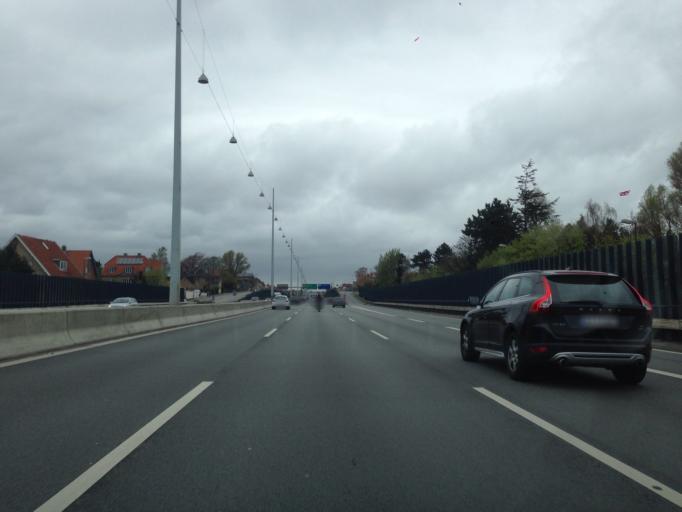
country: DK
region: Capital Region
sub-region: Gentofte Kommune
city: Charlottenlund
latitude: 55.7335
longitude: 12.5444
